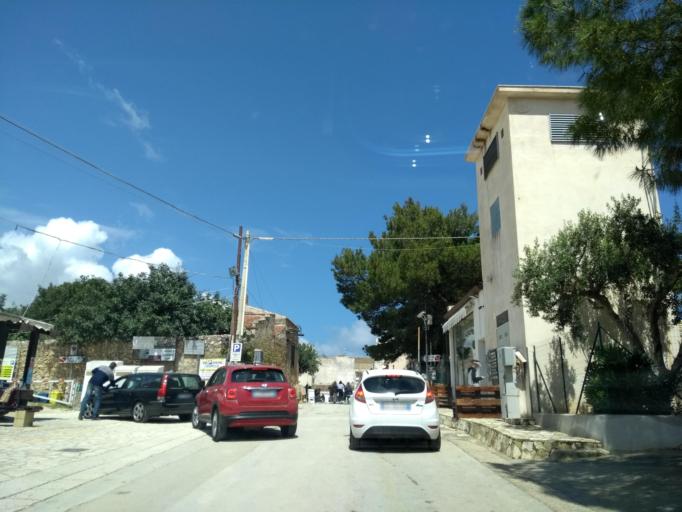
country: IT
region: Sicily
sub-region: Trapani
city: Castelluzzo
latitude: 38.0694
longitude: 12.8182
